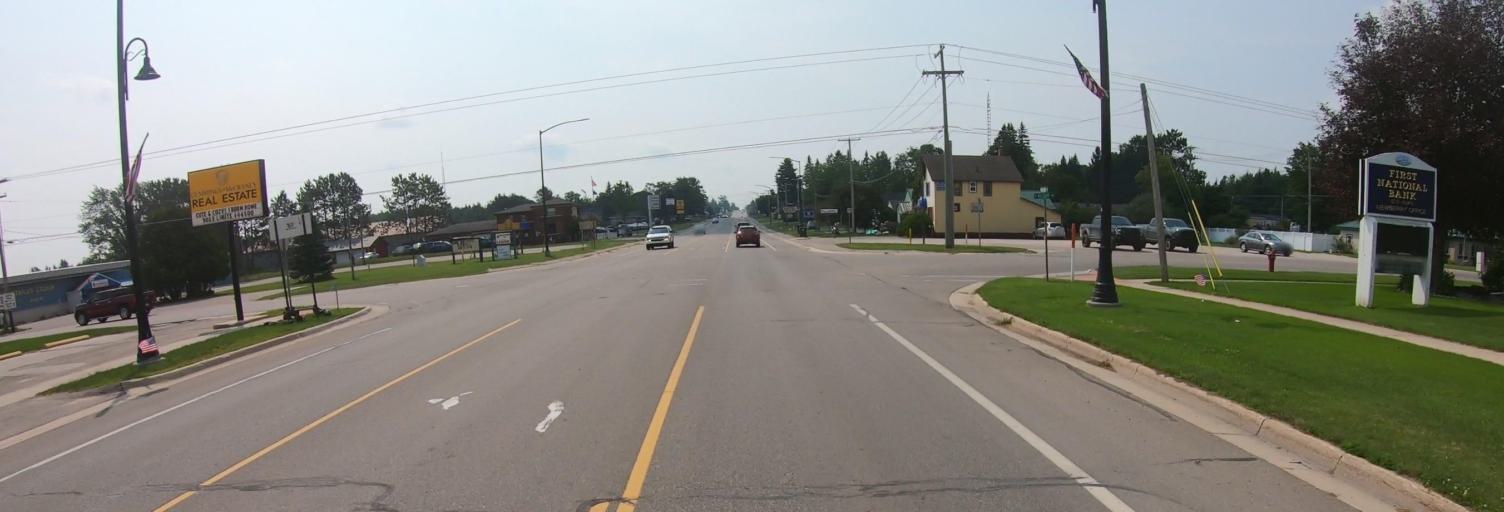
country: US
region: Michigan
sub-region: Luce County
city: Newberry
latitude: 46.3469
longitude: -85.5099
